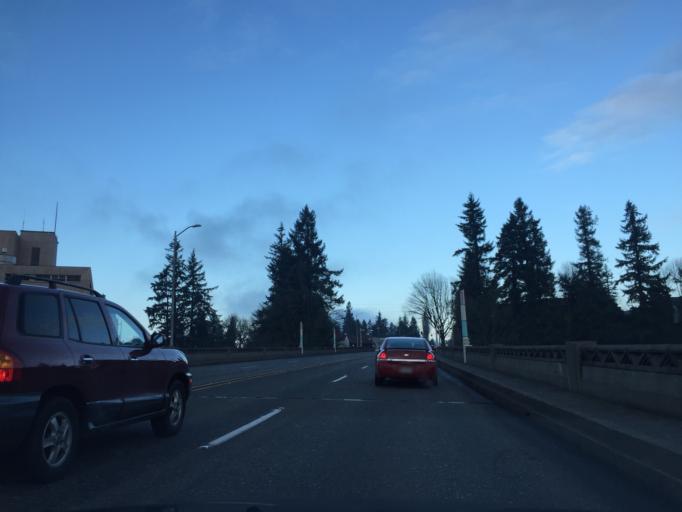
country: US
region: Washington
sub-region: Thurston County
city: Tumwater
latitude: 47.0147
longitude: -122.9028
